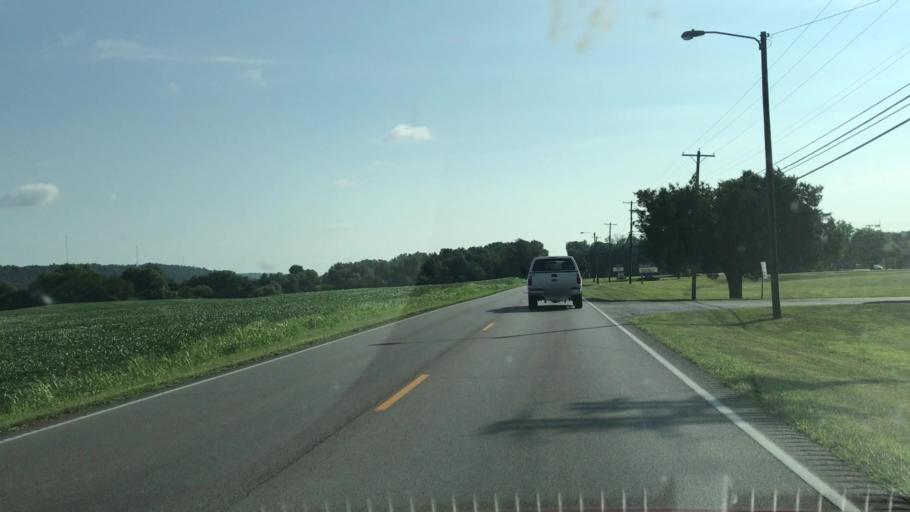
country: US
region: Kentucky
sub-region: Barren County
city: Cave City
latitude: 37.1520
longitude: -85.9345
